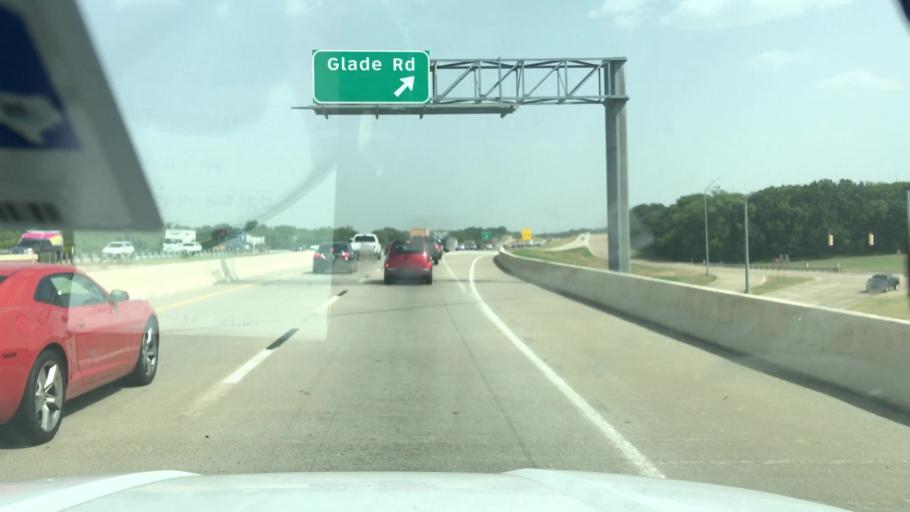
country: US
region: Texas
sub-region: Tarrant County
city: Grapevine
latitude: 32.8918
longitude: -97.0823
